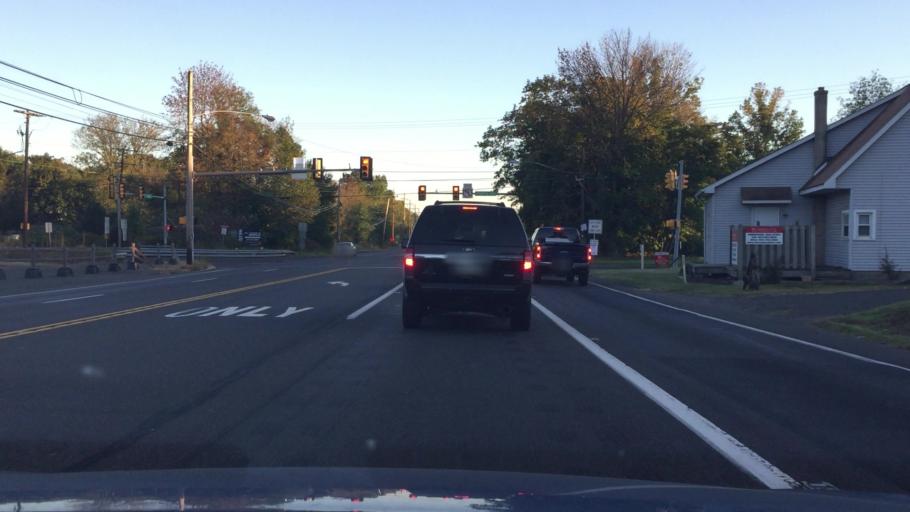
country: US
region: Pennsylvania
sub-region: Lehigh County
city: Coopersburg
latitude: 40.4812
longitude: -75.3753
